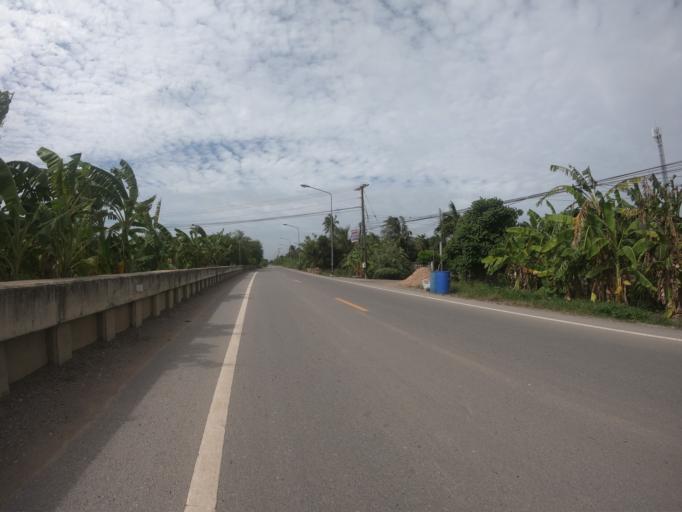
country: TH
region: Pathum Thani
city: Nong Suea
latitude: 14.0481
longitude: 100.8928
